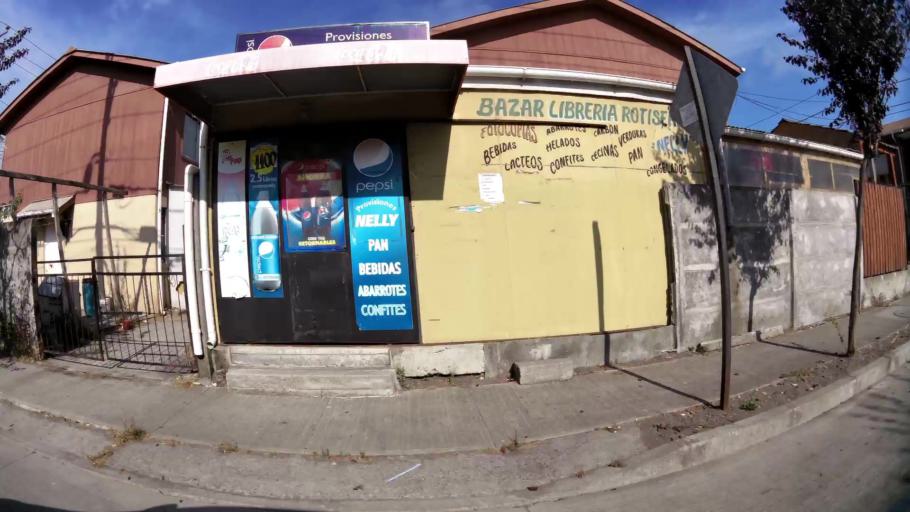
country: CL
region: Biobio
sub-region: Provincia de Concepcion
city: Talcahuano
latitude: -36.7934
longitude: -73.1171
